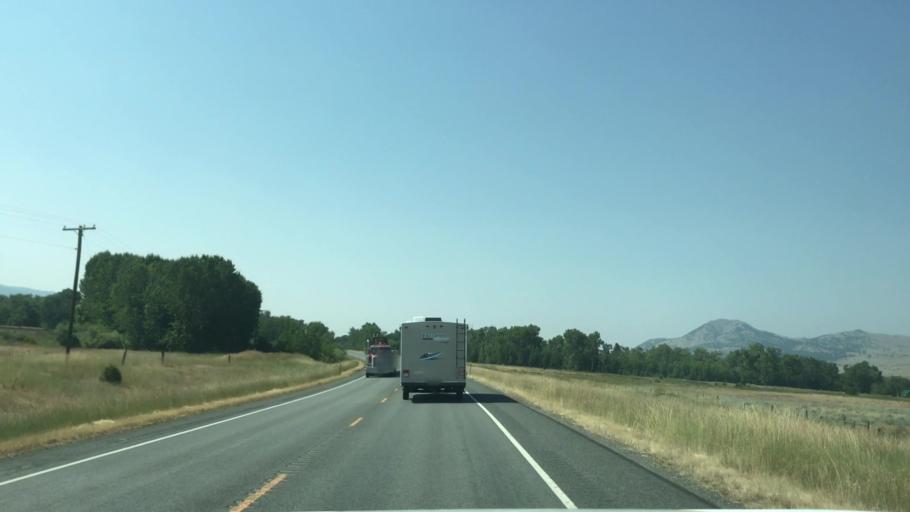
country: US
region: Montana
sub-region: Broadwater County
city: Townsend
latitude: 46.4837
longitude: -111.6652
